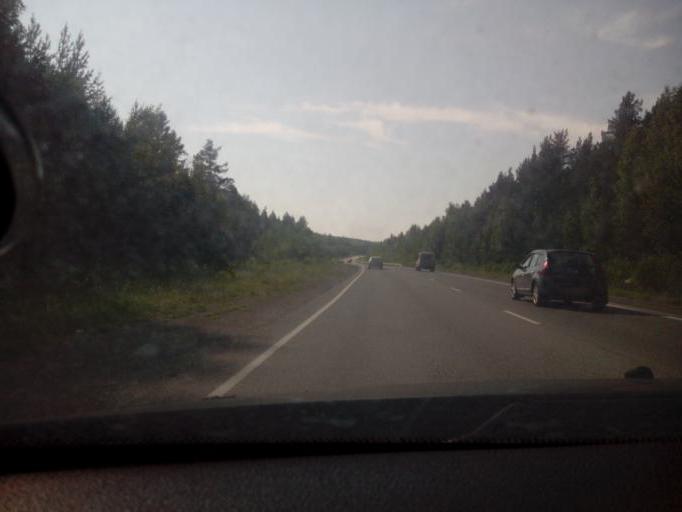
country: RU
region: Sverdlovsk
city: Iset'
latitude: 57.0904
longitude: 60.3882
